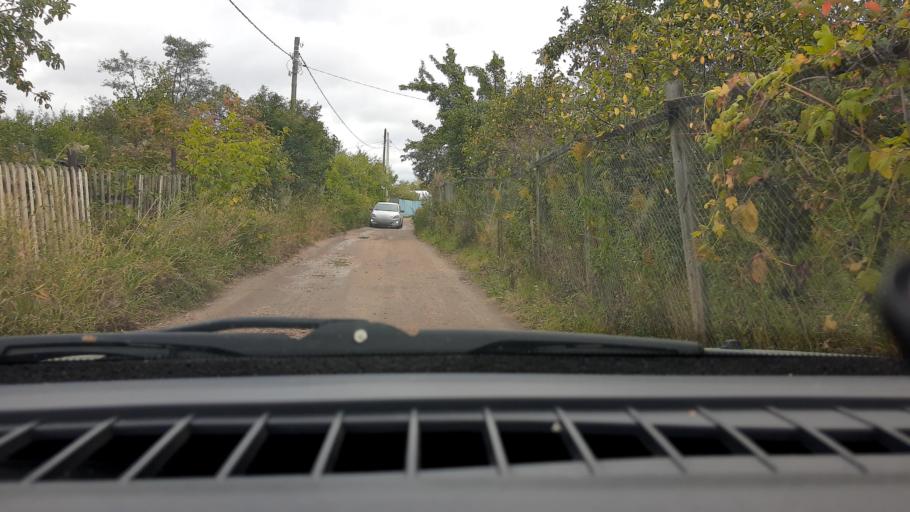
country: RU
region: Nizjnij Novgorod
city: Gorbatovka
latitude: 56.3195
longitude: 43.8372
